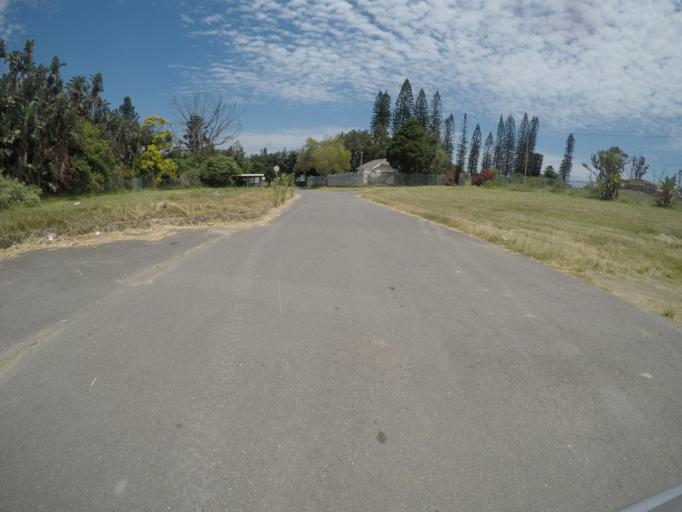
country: ZA
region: Eastern Cape
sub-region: Buffalo City Metropolitan Municipality
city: East London
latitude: -32.9811
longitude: 27.8771
